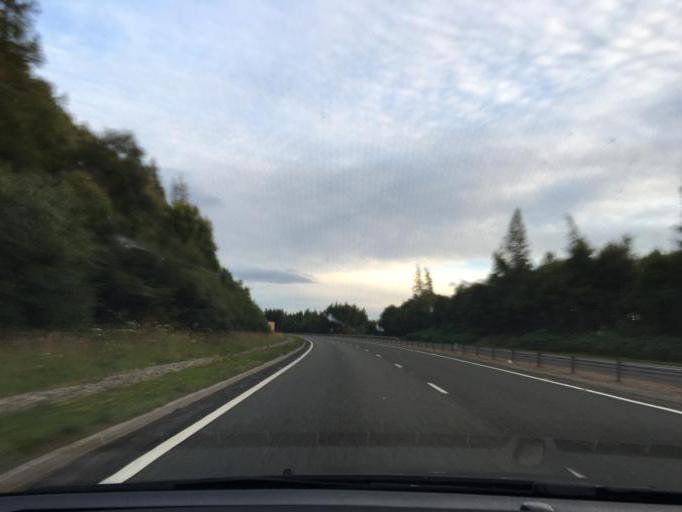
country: GB
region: Scotland
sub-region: Highland
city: Aviemore
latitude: 57.3257
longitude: -3.9778
